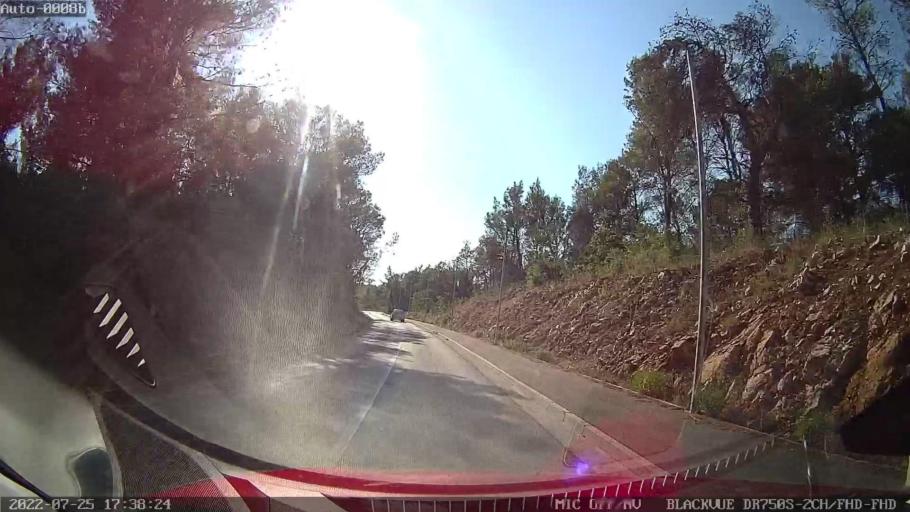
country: HR
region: Zadarska
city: Posedarje
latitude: 44.2094
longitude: 15.4623
